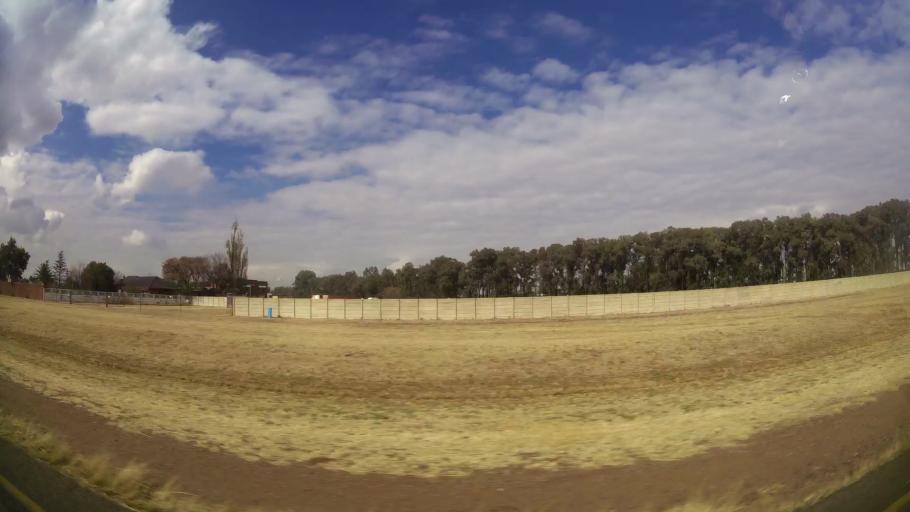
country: ZA
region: Gauteng
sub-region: Sedibeng District Municipality
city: Meyerton
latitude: -26.6415
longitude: 28.0419
